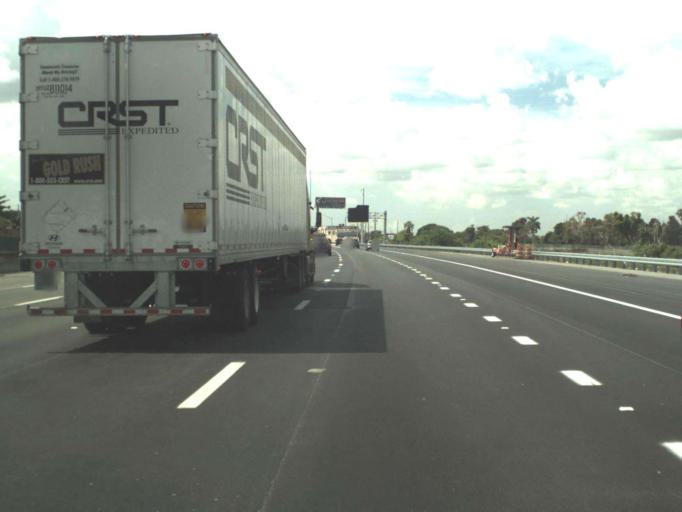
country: US
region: Florida
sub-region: Broward County
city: Pembroke Park
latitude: 26.0043
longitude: -80.1672
